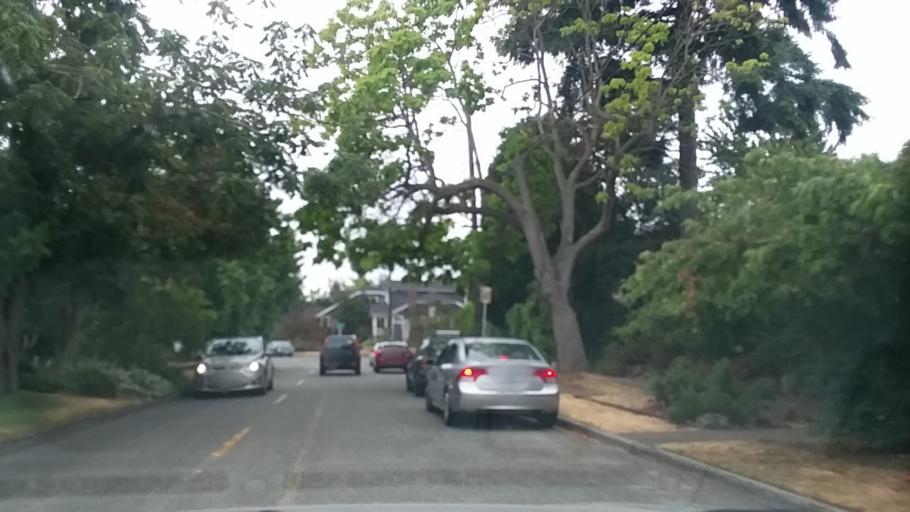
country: US
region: Washington
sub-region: King County
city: Shoreline
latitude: 47.6846
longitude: -122.3472
